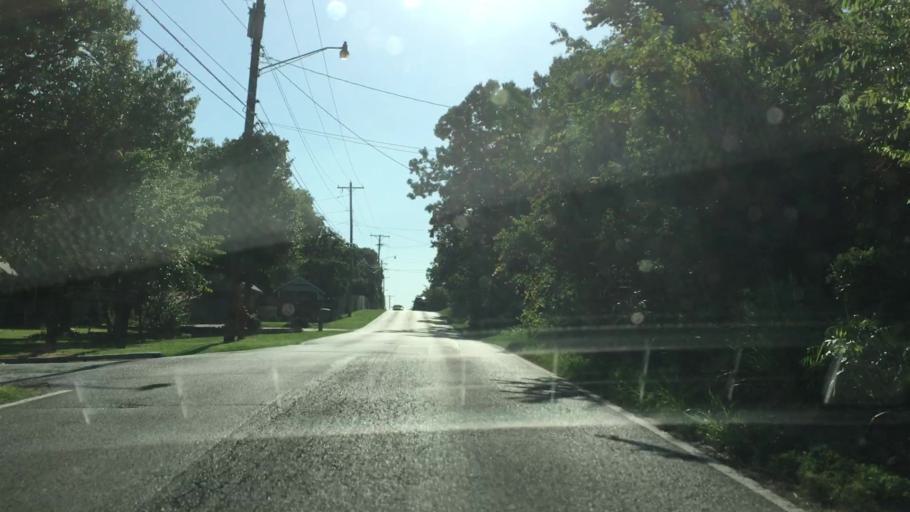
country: US
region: Oklahoma
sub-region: Cherokee County
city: Tahlequah
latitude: 35.9008
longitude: -94.9658
